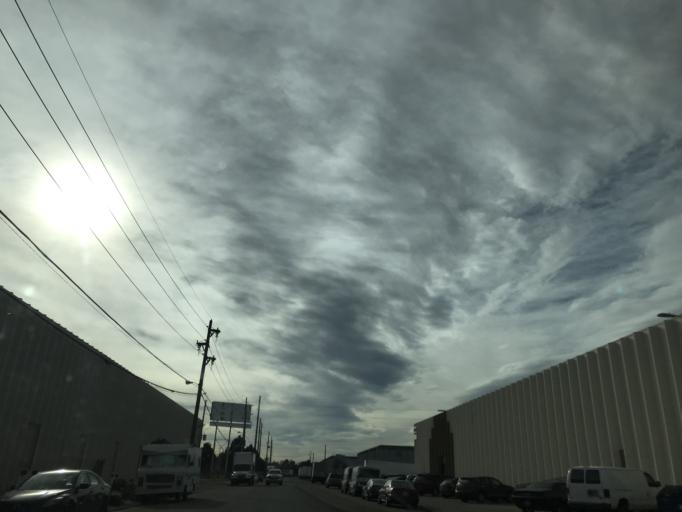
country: US
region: Colorado
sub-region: Adams County
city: Commerce City
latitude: 39.7765
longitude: -104.9082
